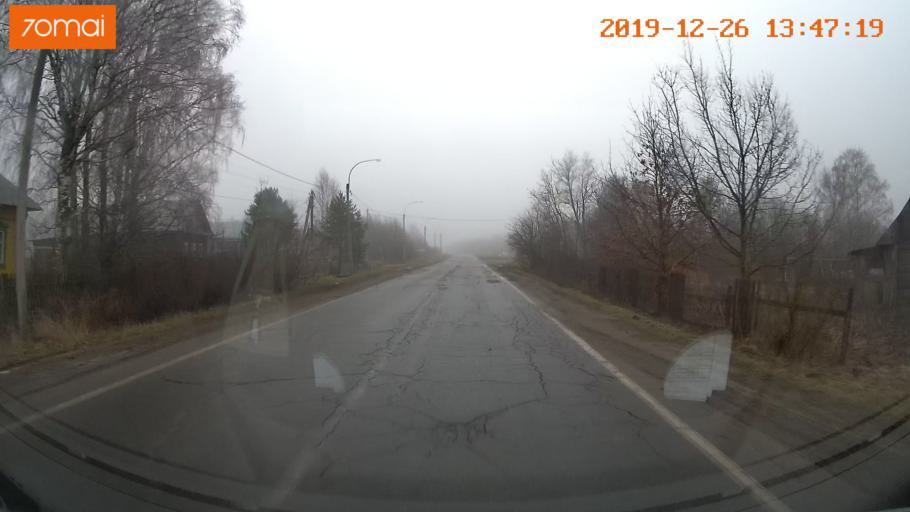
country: RU
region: Vologda
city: Sheksna
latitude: 58.6857
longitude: 38.5330
